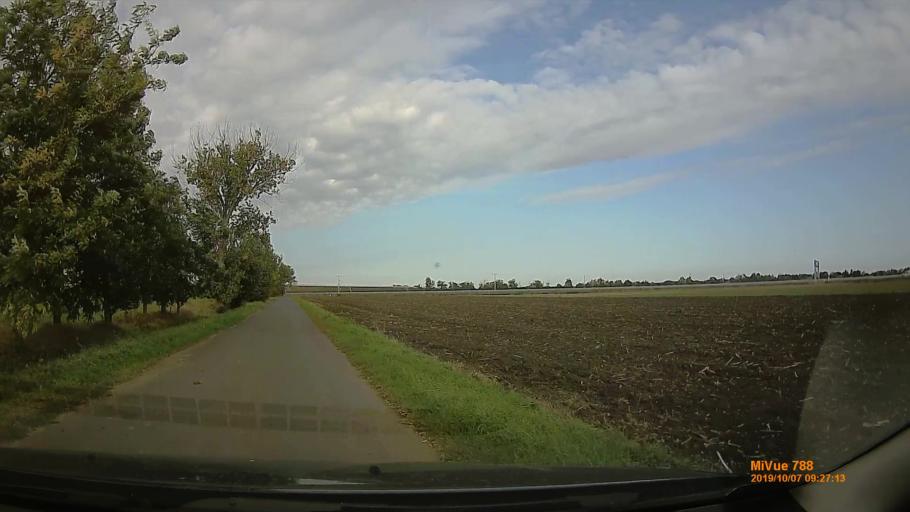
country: HU
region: Bekes
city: Szarvas
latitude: 46.8113
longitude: 20.6546
